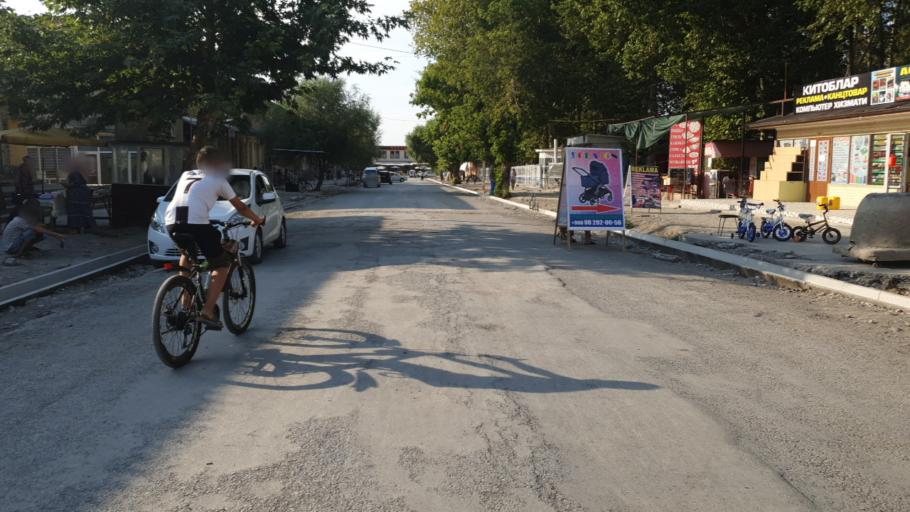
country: UZ
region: Fergana
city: Yaypan
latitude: 40.3792
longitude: 70.8107
